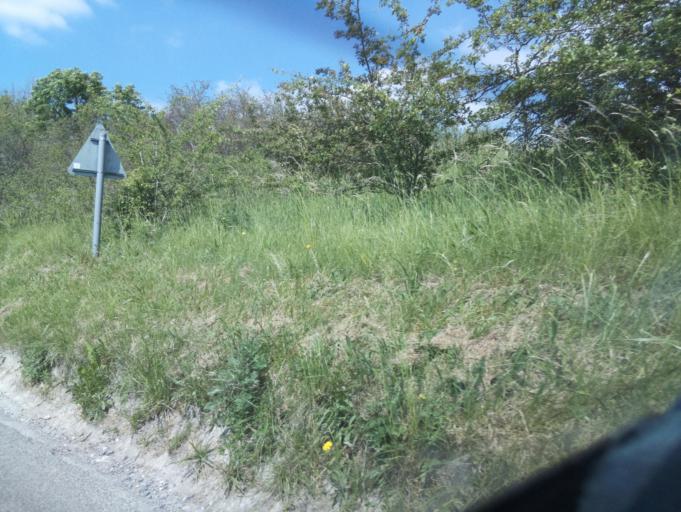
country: GB
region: England
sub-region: Wiltshire
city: Rushall
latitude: 51.2847
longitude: -1.8023
